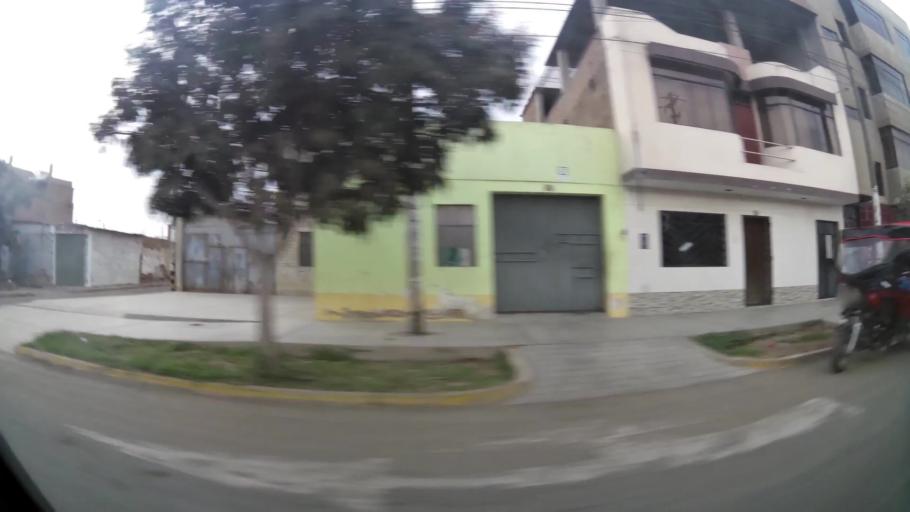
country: PE
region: La Libertad
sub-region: Provincia de Trujillo
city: El Porvenir
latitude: -8.0883
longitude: -79.0159
